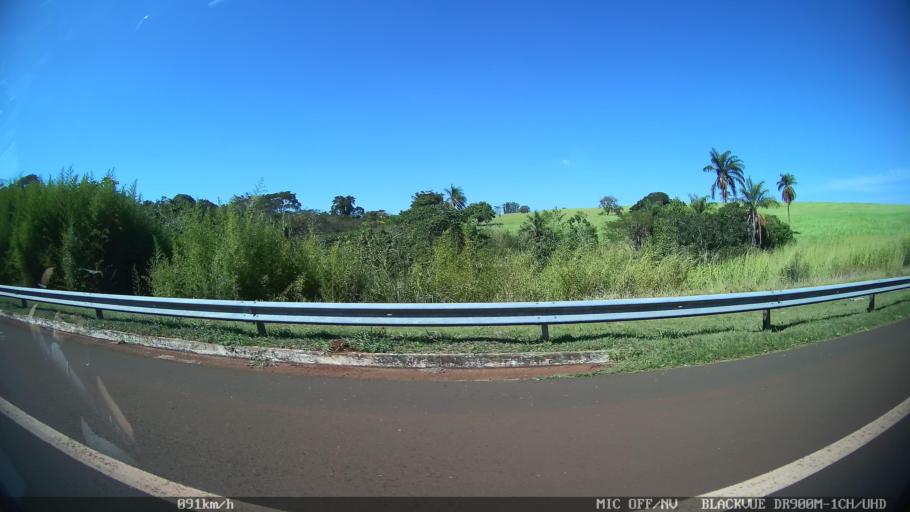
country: BR
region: Sao Paulo
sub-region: Franca
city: Franca
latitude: -20.6354
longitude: -47.4702
